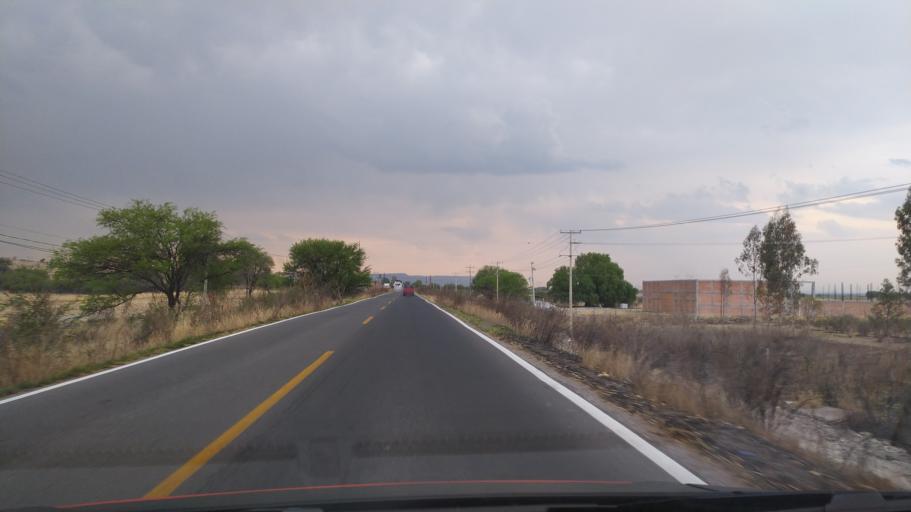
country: MX
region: Guanajuato
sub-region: San Francisco del Rincon
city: San Ignacio de Hidalgo
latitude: 20.8223
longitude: -101.9021
